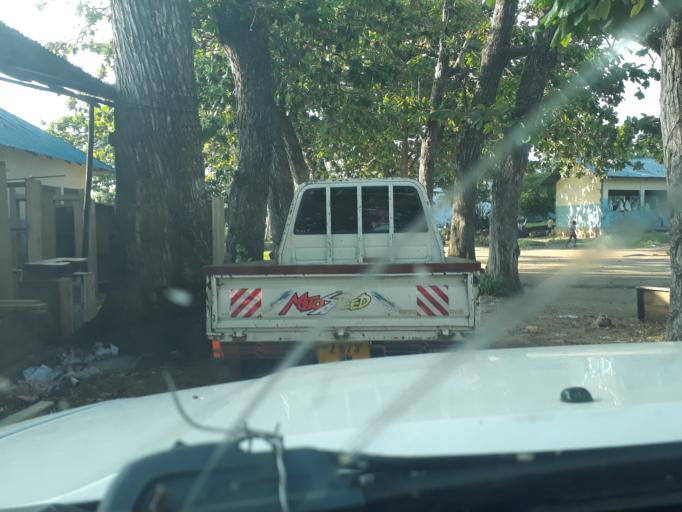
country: TZ
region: Zanzibar North
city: Mkokotoni
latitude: -5.8744
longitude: 39.2574
